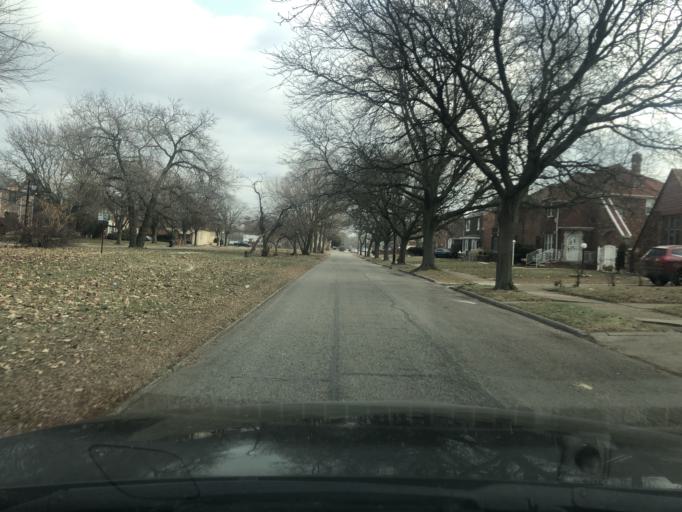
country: US
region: Michigan
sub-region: Wayne County
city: Highland Park
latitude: 42.3954
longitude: -83.1261
